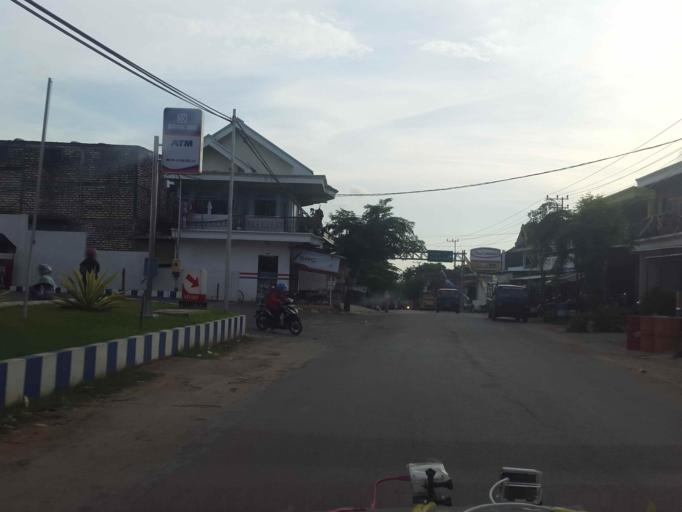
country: ID
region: East Java
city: Senmasen
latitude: -6.9981
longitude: 113.8662
